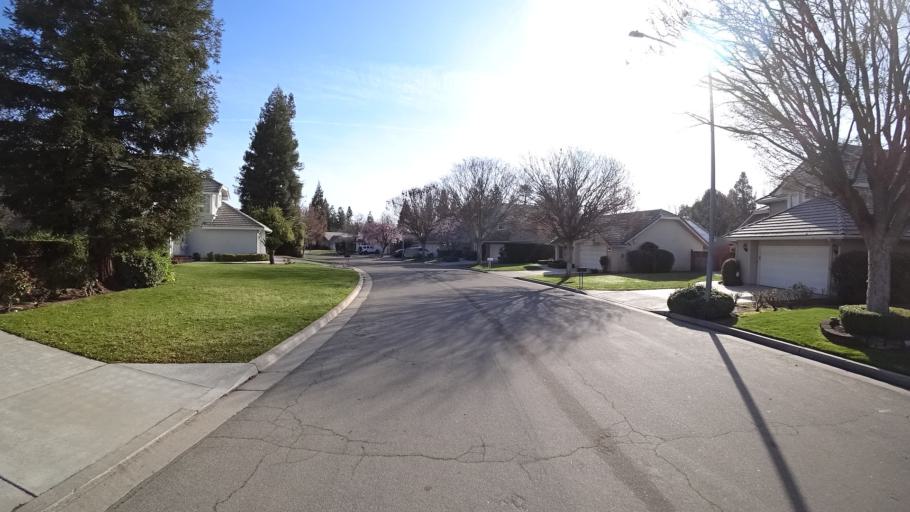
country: US
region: California
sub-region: Fresno County
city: Clovis
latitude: 36.8690
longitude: -119.7611
